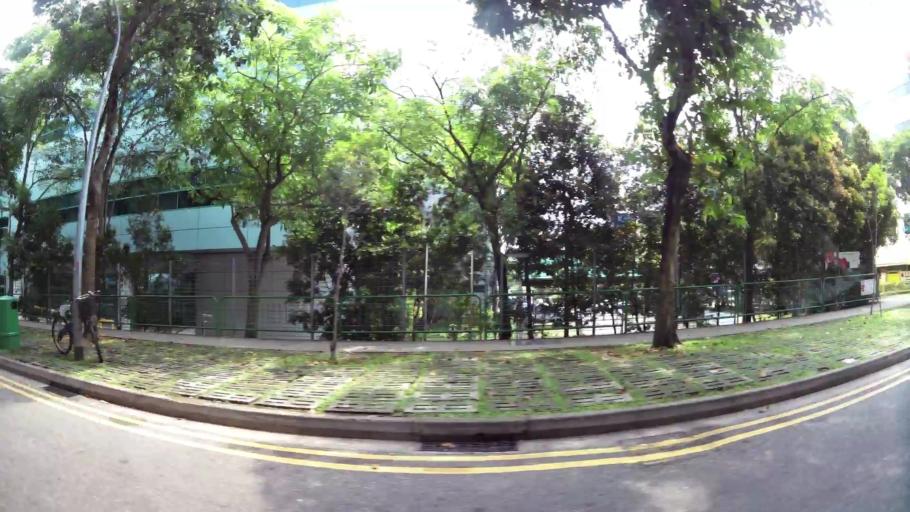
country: SG
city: Singapore
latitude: 1.3372
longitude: 103.9090
